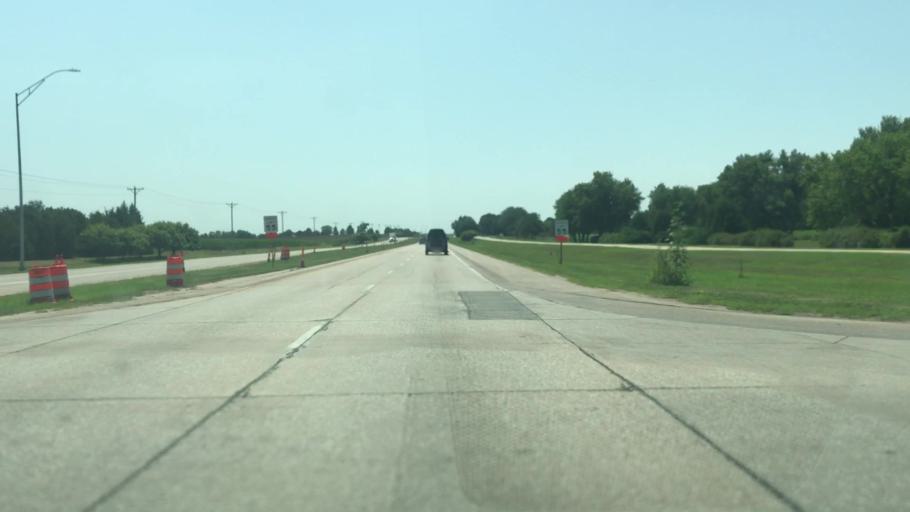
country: US
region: Nebraska
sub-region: Adams County
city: Hastings
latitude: 40.6406
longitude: -98.3820
